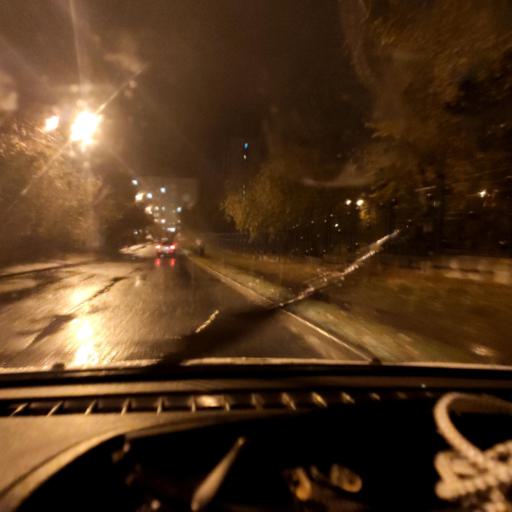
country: RU
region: Samara
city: Zhigulevsk
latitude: 53.4816
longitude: 49.4684
